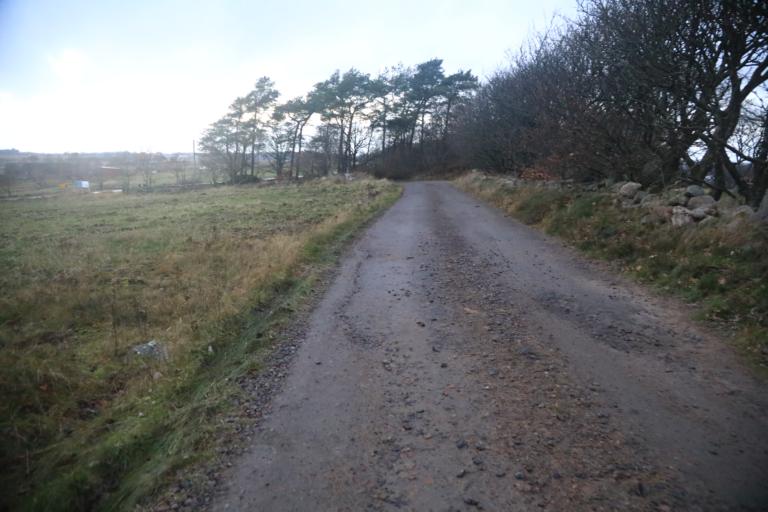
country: SE
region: Halland
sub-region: Varbergs Kommun
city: Traslovslage
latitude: 57.1109
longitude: 12.3257
